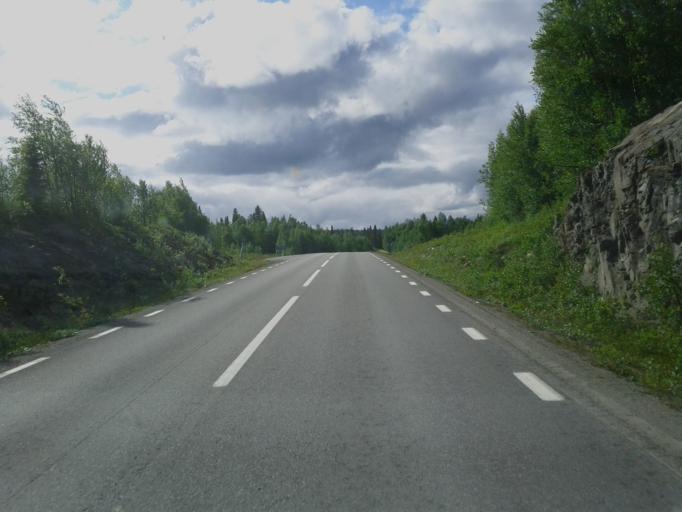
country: NO
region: Nordland
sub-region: Rana
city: Mo i Rana
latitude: 65.7121
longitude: 15.2248
